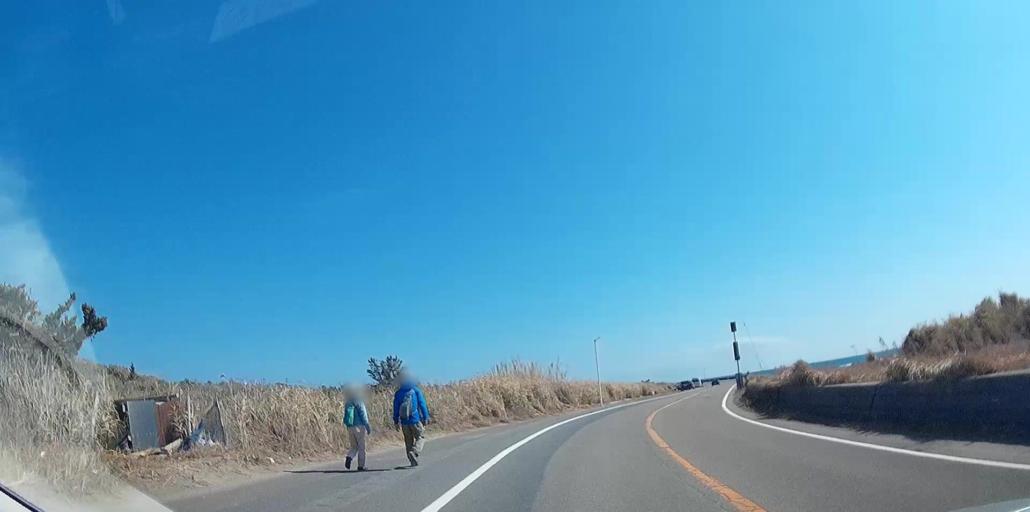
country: JP
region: Chiba
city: Tateyama
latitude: 34.9044
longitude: 139.8426
